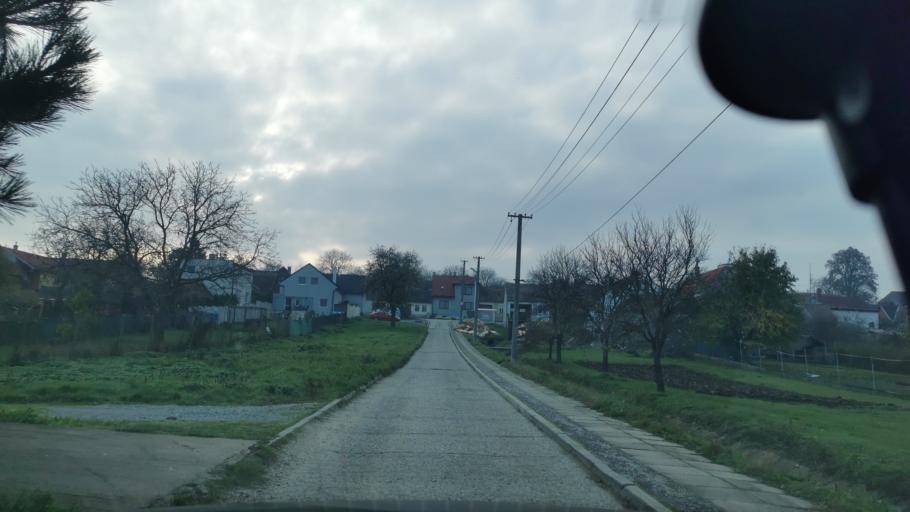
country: SK
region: Trnavsky
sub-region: Okres Skalica
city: Skalica
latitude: 48.7643
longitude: 17.2827
